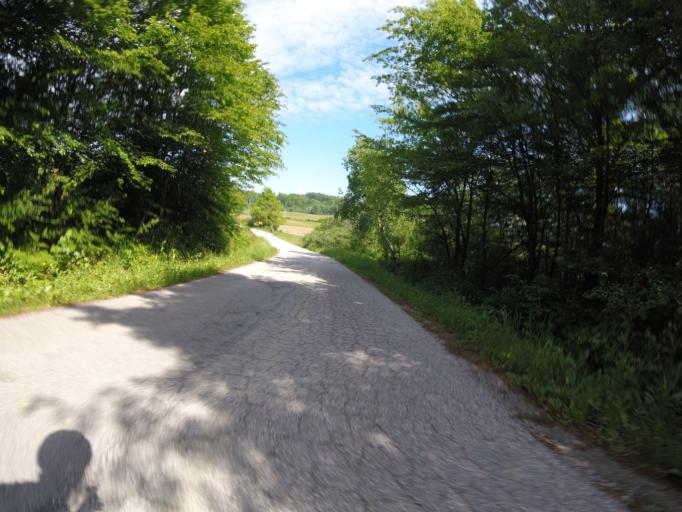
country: HR
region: Zagrebacka
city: Lukavec
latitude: 45.5824
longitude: 16.0028
